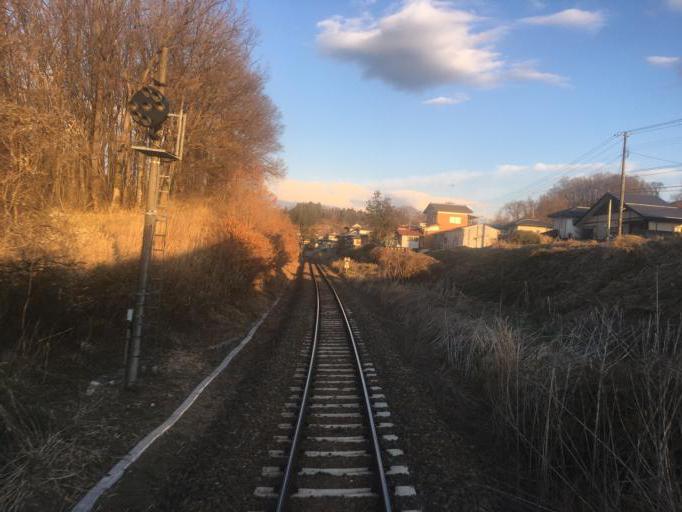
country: JP
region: Fukushima
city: Koriyama
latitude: 37.4173
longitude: 140.4295
